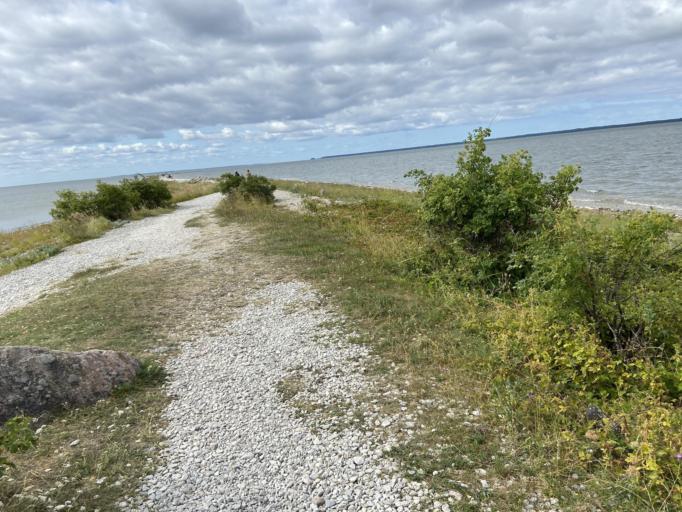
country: EE
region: Hiiumaa
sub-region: Kaerdla linn
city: Kardla
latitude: 58.7598
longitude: 22.7954
